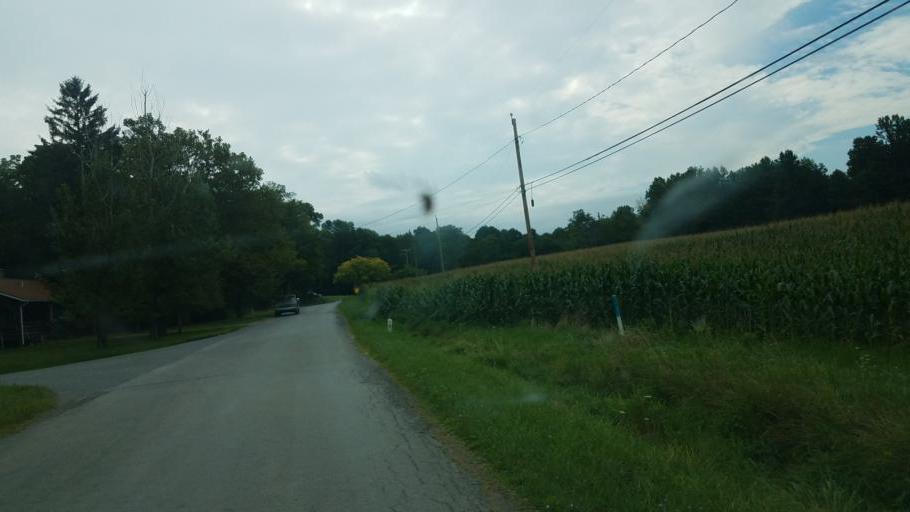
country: US
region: Pennsylvania
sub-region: Erie County
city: Lake City
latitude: 42.0023
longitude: -80.4337
